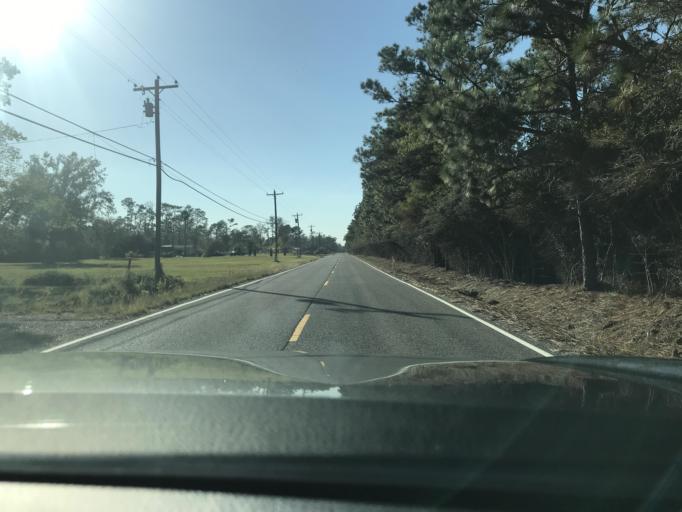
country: US
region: Louisiana
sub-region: Calcasieu Parish
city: Moss Bluff
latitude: 30.3225
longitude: -93.2704
